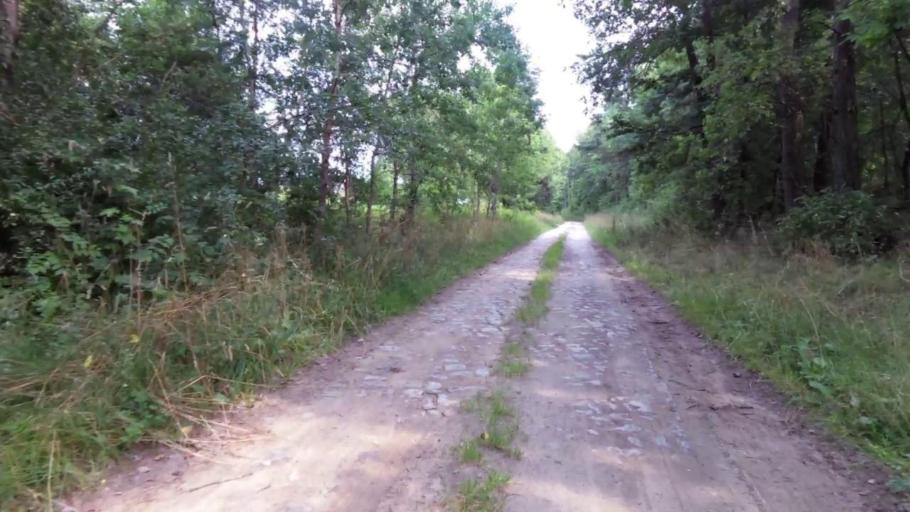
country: PL
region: West Pomeranian Voivodeship
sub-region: Powiat drawski
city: Drawsko Pomorskie
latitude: 53.5662
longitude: 15.8527
